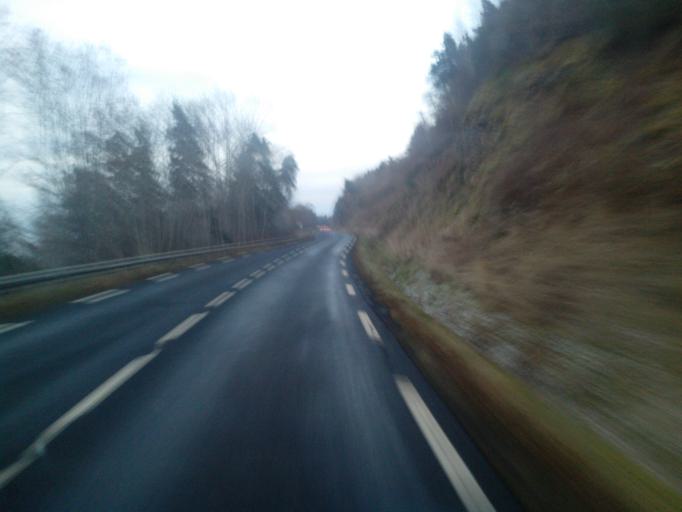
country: FR
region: Auvergne
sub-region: Departement du Cantal
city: Murat
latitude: 45.1030
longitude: 2.9079
